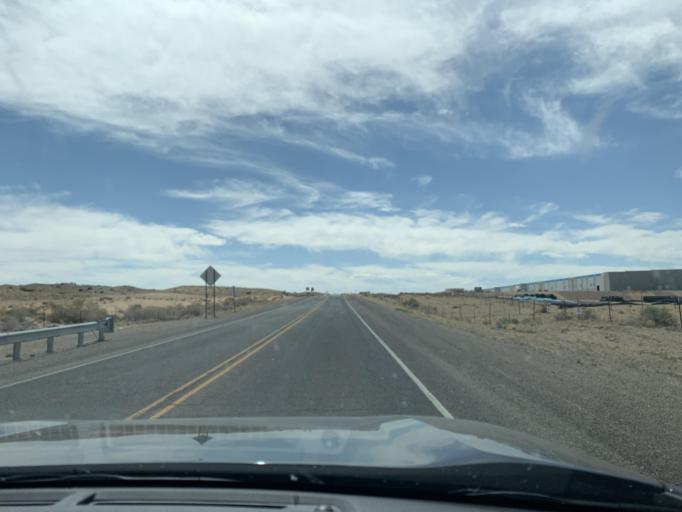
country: US
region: New Mexico
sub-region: Valencia County
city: Los Lunas
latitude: 34.8237
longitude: -106.8078
